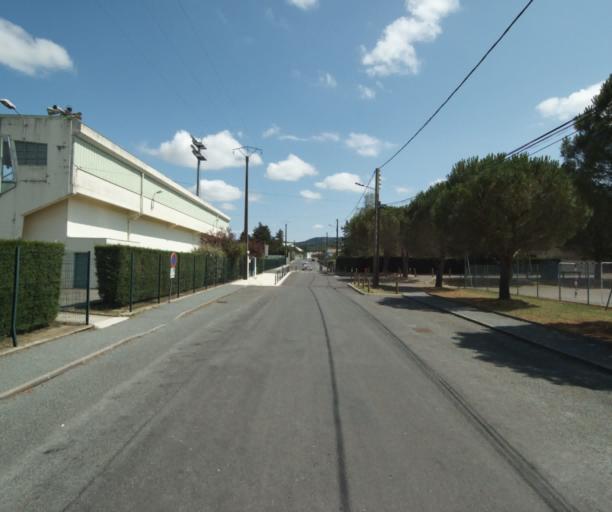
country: FR
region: Midi-Pyrenees
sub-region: Departement de la Haute-Garonne
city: Revel
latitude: 43.4525
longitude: 2.0131
